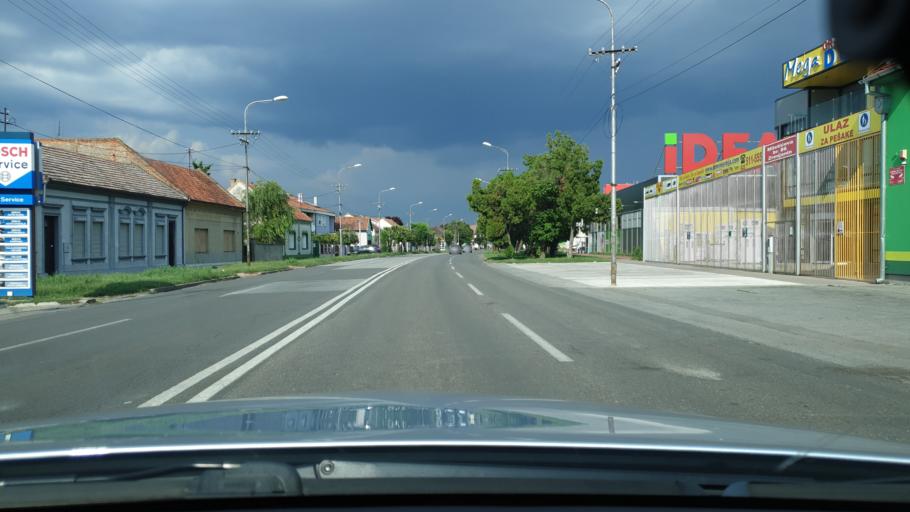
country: RS
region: Autonomna Pokrajina Vojvodina
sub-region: Srednjebanatski Okrug
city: Zrenjanin
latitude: 45.3834
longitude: 20.4072
